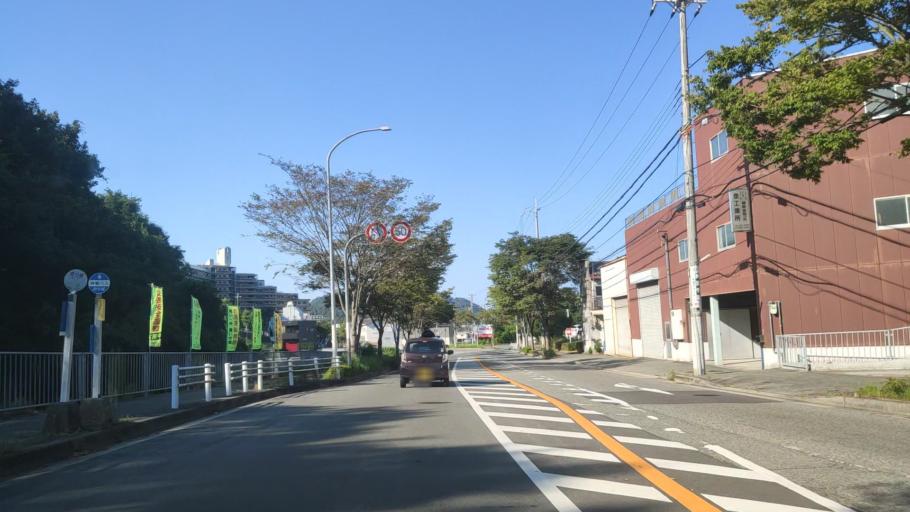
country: JP
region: Hyogo
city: Kobe
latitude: 34.7706
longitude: 135.1897
